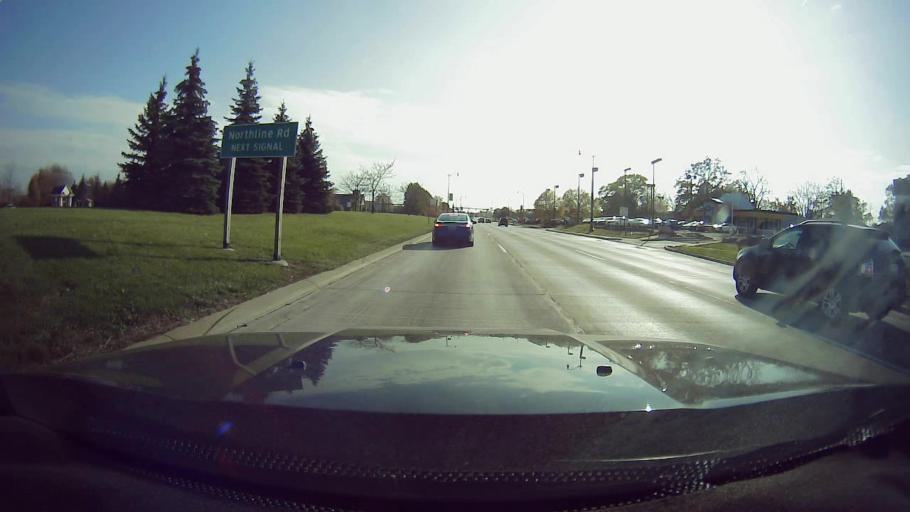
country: US
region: Michigan
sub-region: Wayne County
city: Taylor
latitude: 42.2137
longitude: -83.2690
